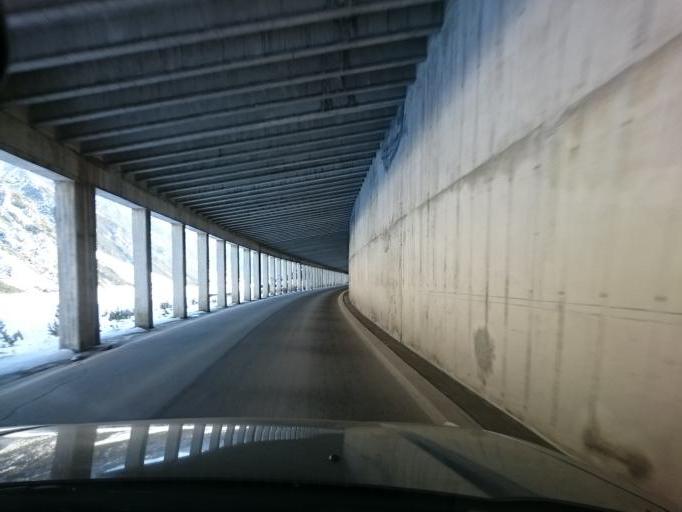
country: IT
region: Lombardy
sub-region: Provincia di Sondrio
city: Livigno
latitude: 46.6008
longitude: 10.1735
